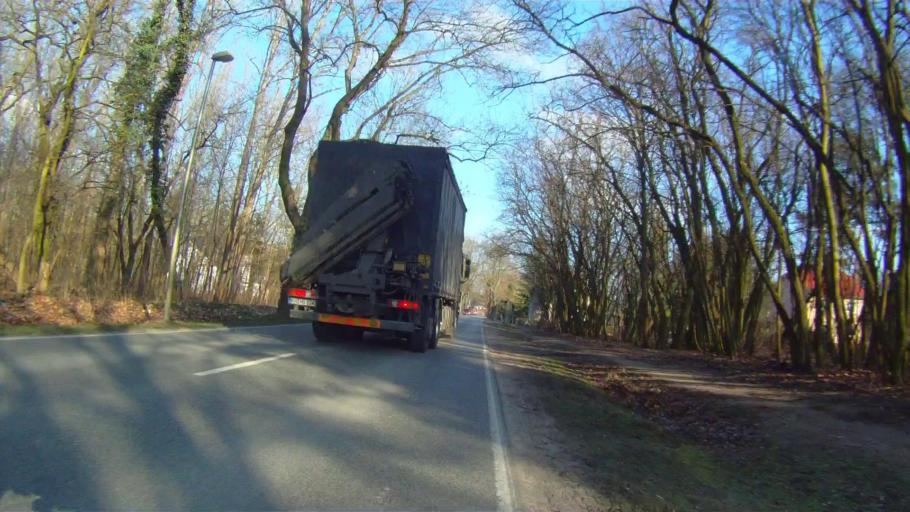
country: DE
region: Brandenburg
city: Woltersdorf
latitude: 52.4576
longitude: 13.7563
